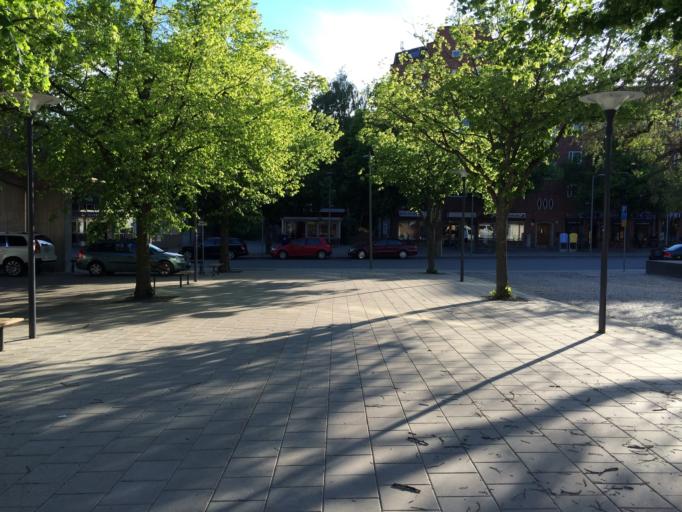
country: SE
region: Stockholm
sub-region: Huddinge Kommun
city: Segeltorp
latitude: 59.2924
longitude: 17.9690
